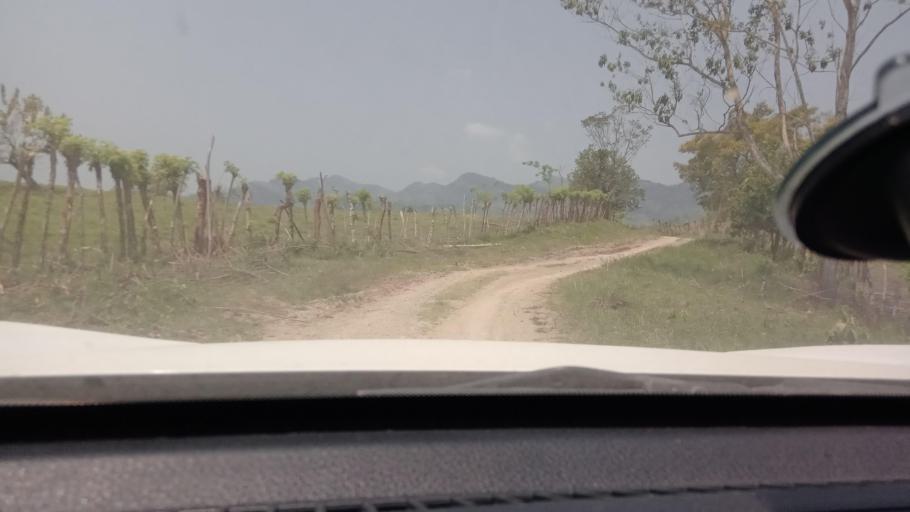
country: MX
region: Tabasco
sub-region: Huimanguillo
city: Francisco Rueda
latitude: 17.4851
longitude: -93.9353
